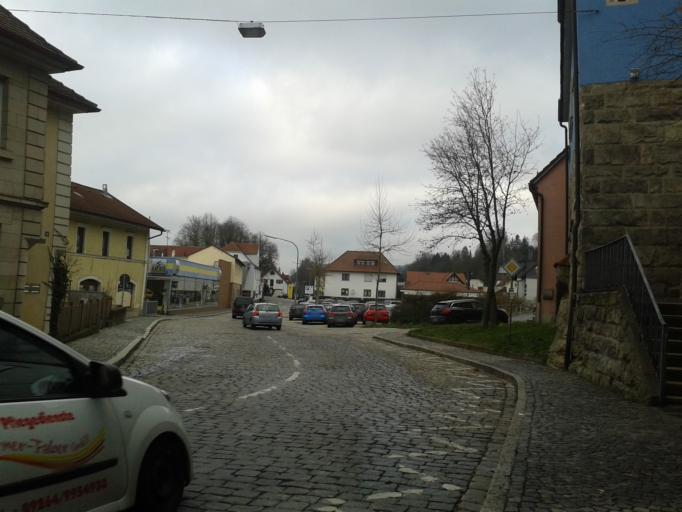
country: DE
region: Bavaria
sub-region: Upper Franconia
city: Kronach
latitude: 50.2426
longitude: 11.3237
